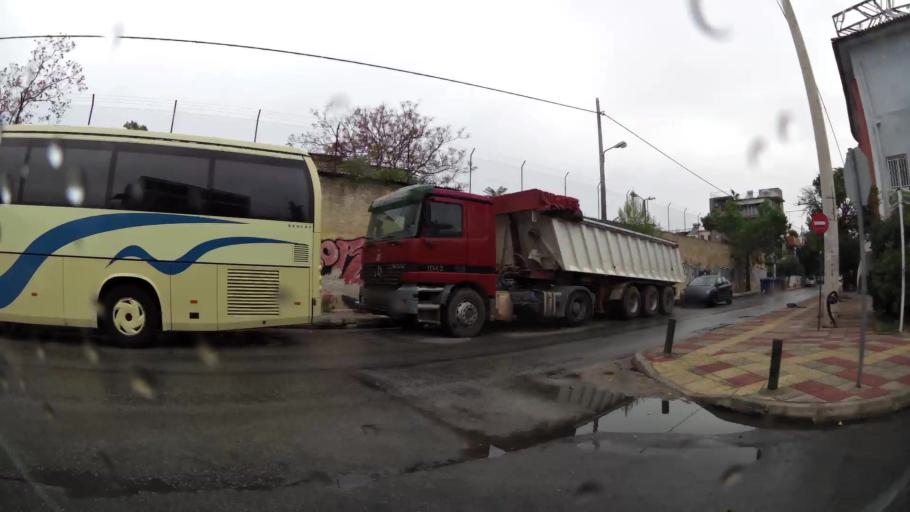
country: GR
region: Attica
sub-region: Nomarchia Athinas
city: Ymittos
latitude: 37.9533
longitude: 23.7452
